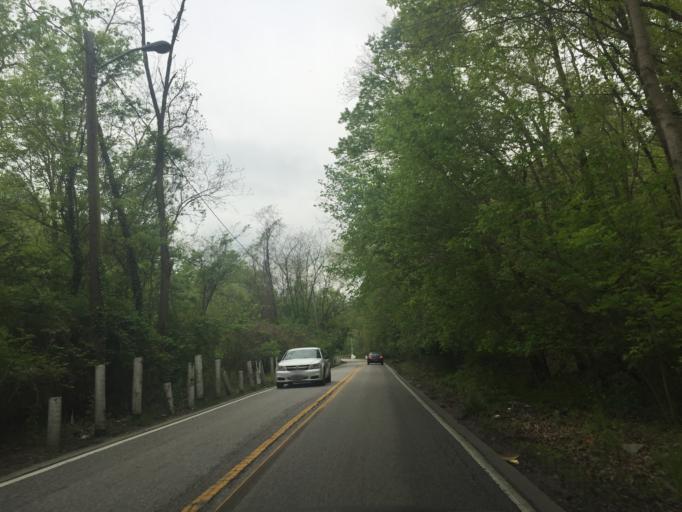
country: US
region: Maryland
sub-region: Baltimore County
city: Charlestown
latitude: 39.3050
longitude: -76.6774
